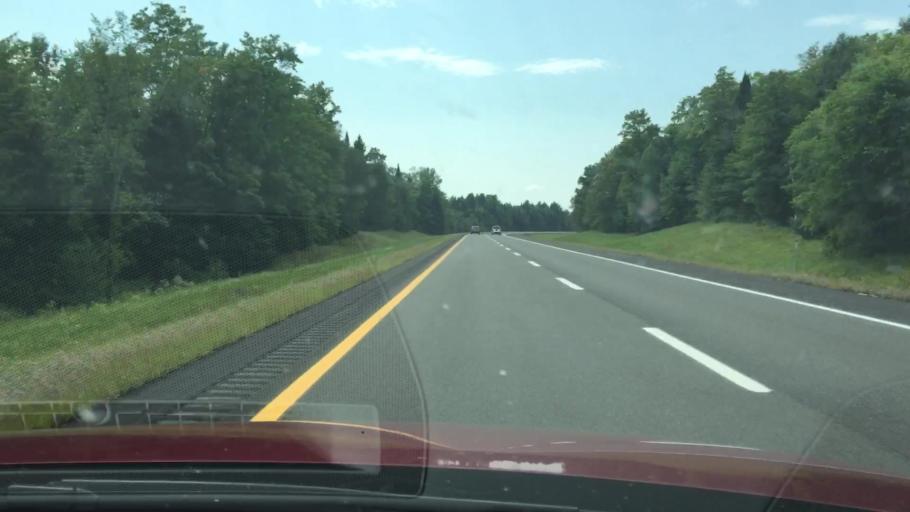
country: US
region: Maine
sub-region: Penobscot County
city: Patten
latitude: 46.0547
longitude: -68.2400
